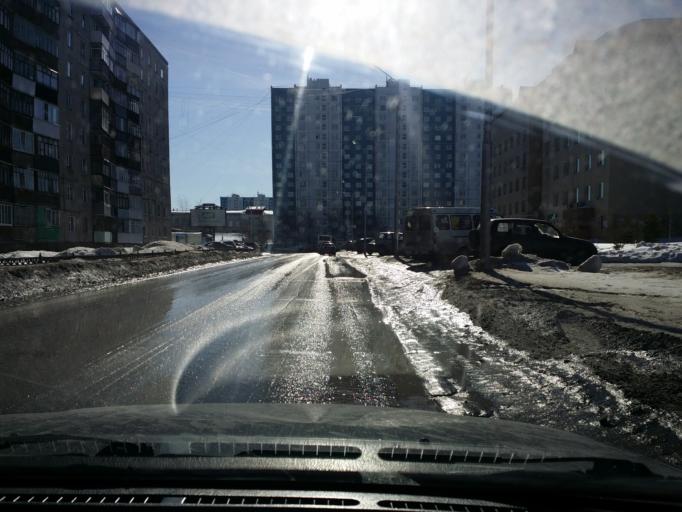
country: RU
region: Khanty-Mansiyskiy Avtonomnyy Okrug
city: Nizhnevartovsk
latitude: 60.9371
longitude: 76.6077
